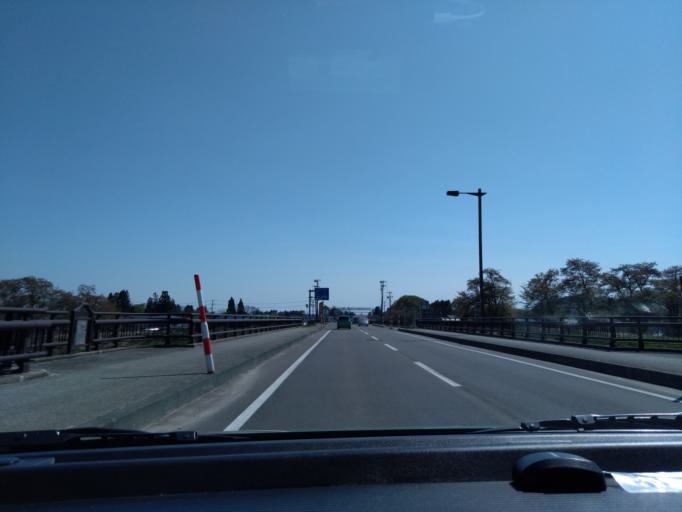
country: JP
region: Akita
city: Kakunodatemachi
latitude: 39.5793
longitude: 140.5674
